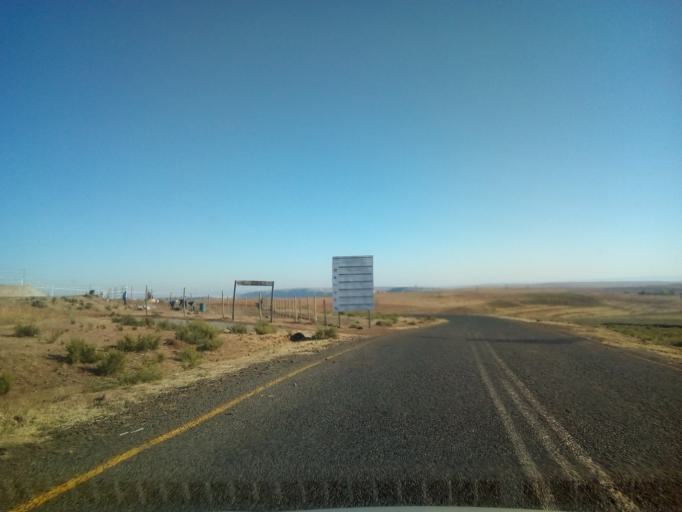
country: LS
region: Berea
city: Teyateyaneng
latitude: -29.2534
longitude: 27.7405
